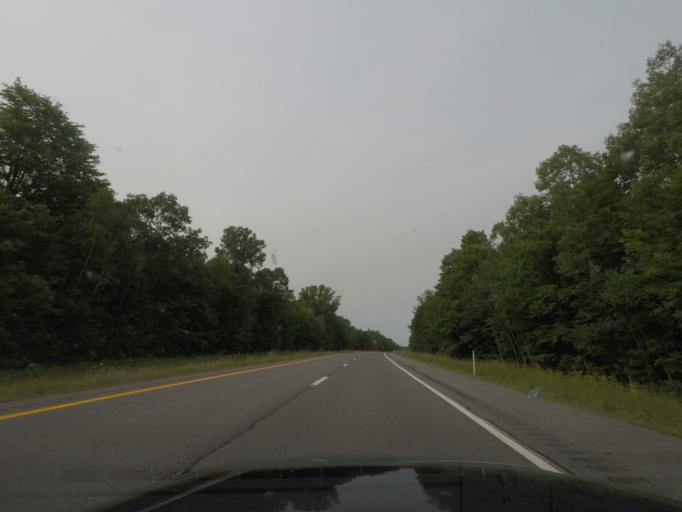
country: US
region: New York
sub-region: Clinton County
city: Champlain
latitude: 44.9015
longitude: -73.4540
